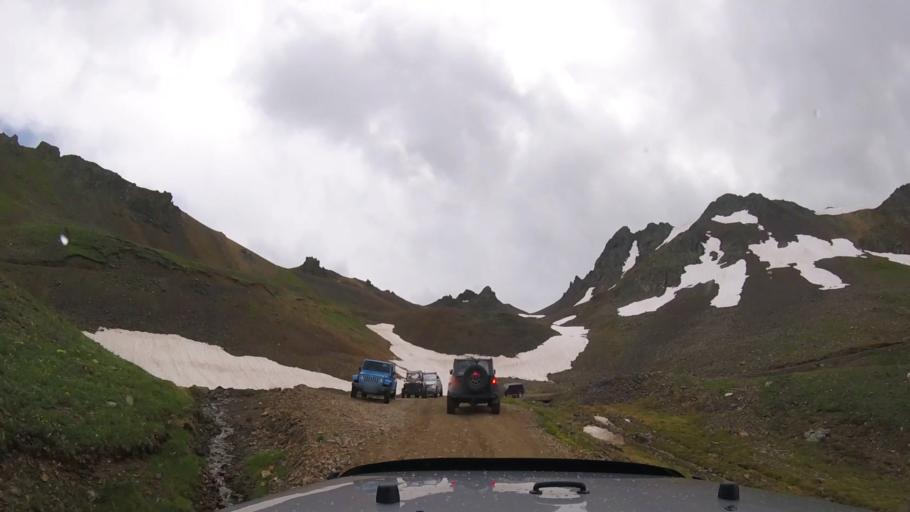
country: US
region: Colorado
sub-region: Ouray County
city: Ouray
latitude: 37.9193
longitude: -107.6200
